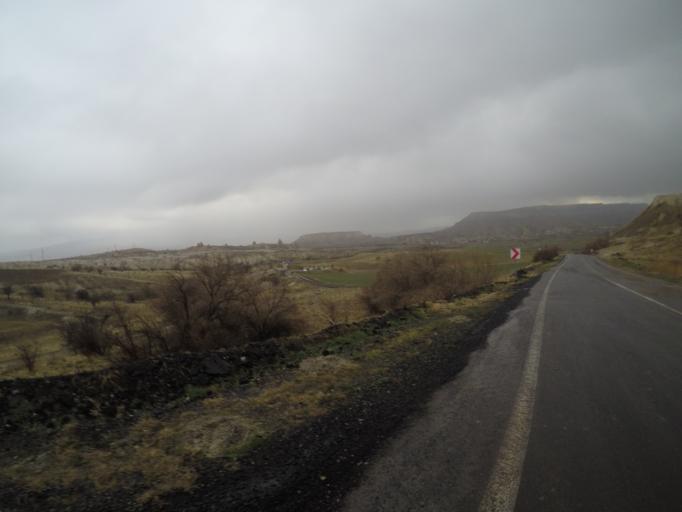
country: TR
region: Nevsehir
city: Goereme
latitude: 38.6671
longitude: 34.8212
